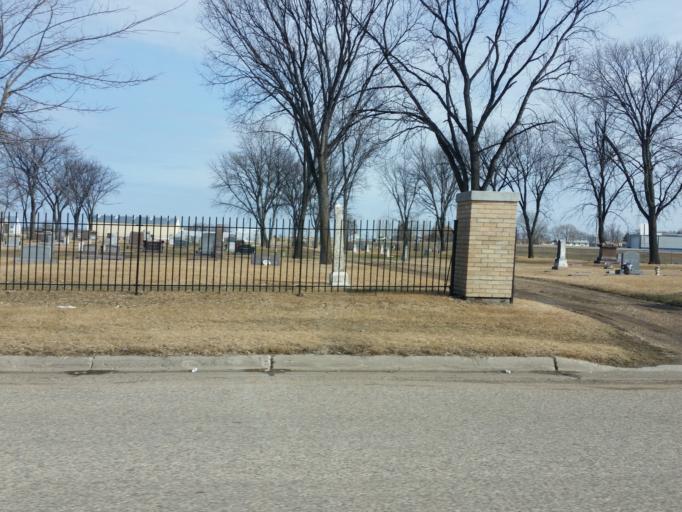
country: US
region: North Dakota
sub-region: Walsh County
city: Grafton
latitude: 48.4128
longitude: -97.4025
